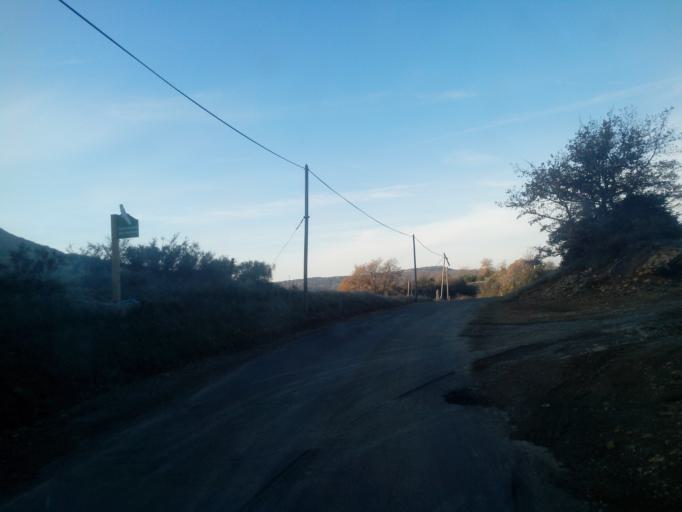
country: FR
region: Languedoc-Roussillon
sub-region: Departement de l'Aude
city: Couiza
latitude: 42.8790
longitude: 2.3292
